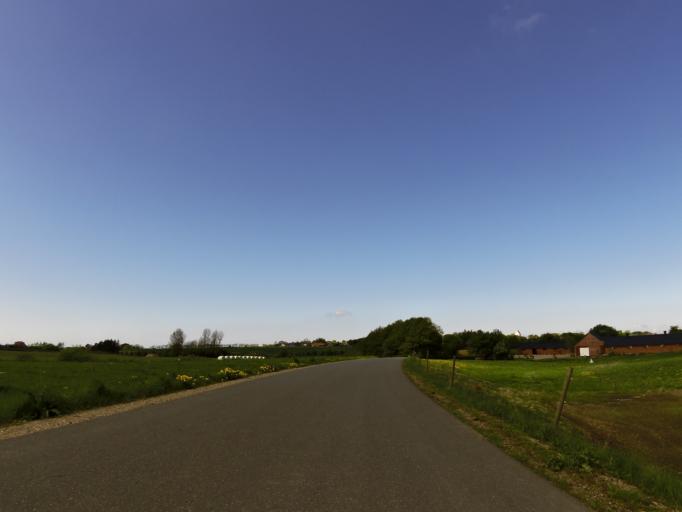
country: DK
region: Central Jutland
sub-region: Holstebro Kommune
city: Vinderup
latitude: 56.4265
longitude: 8.7806
